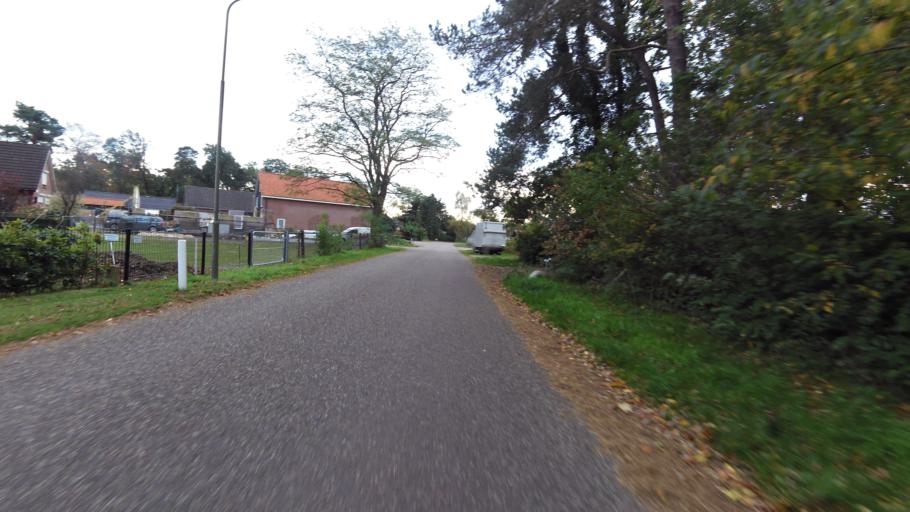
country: NL
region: Gelderland
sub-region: Gemeente Oldebroek
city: Oldebroek
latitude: 52.4418
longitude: 5.9488
